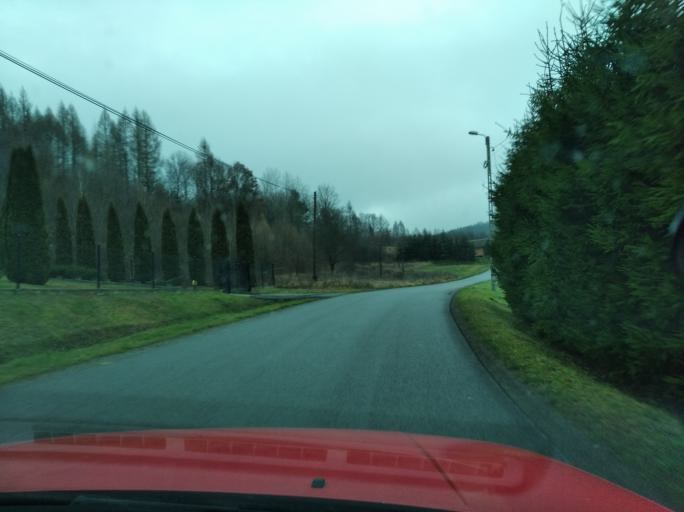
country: PL
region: Subcarpathian Voivodeship
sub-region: Powiat przemyski
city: Nienadowa
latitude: 49.8537
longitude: 22.4228
